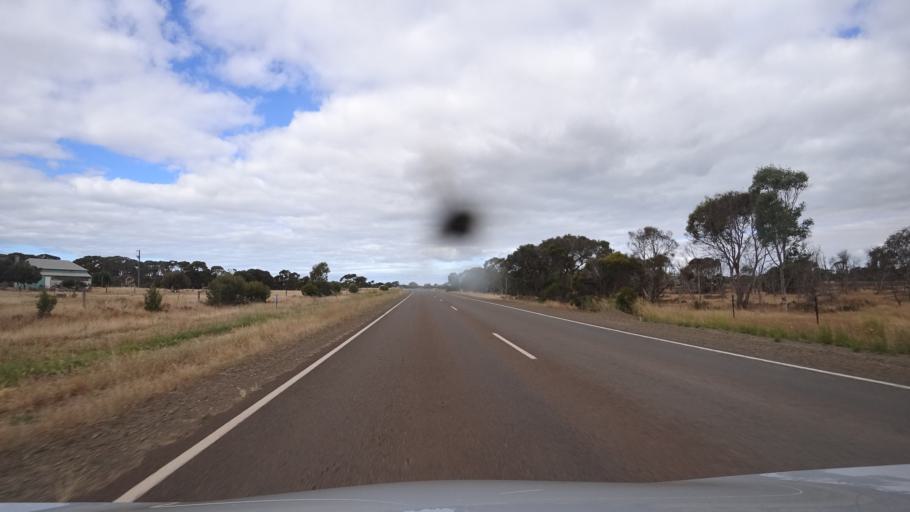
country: AU
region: South Australia
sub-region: Kangaroo Island
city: Kingscote
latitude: -35.6792
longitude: 137.5689
